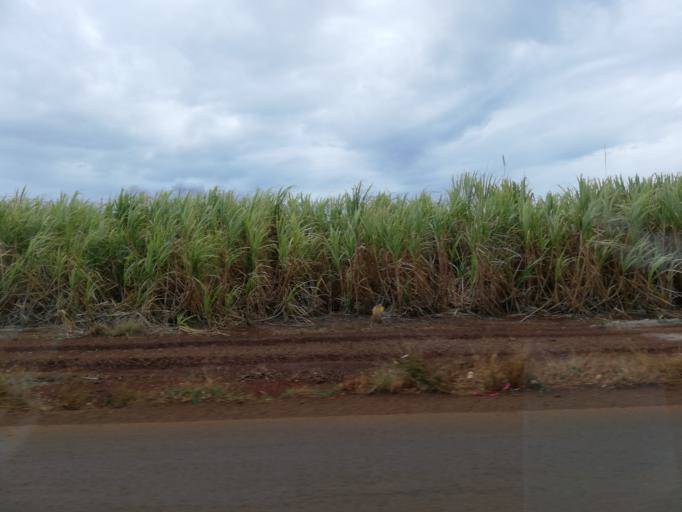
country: MU
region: Black River
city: Petite Riviere
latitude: -20.2119
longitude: 57.4553
